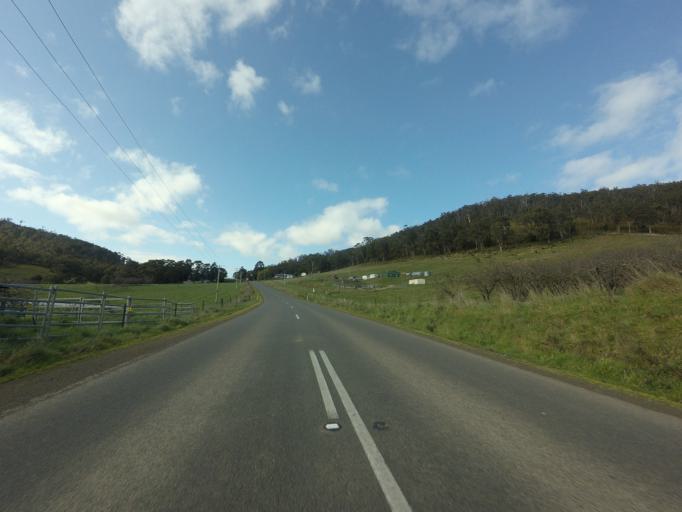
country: AU
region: Tasmania
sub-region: Huon Valley
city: Geeveston
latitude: -43.1735
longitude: 146.9453
